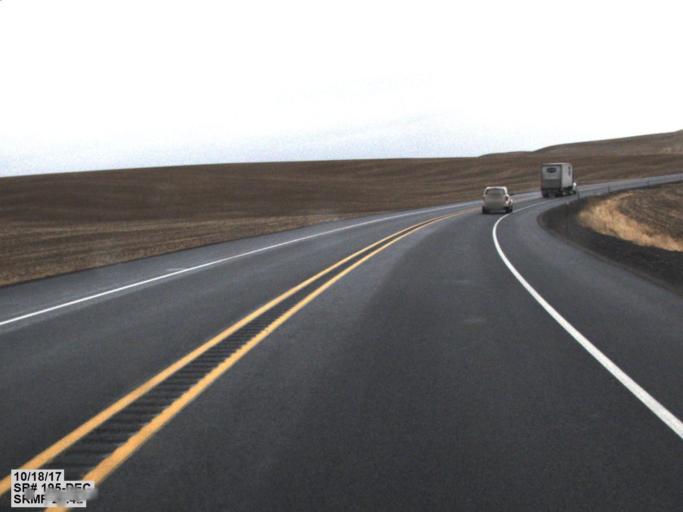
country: US
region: Washington
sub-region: Whitman County
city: Pullman
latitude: 46.7592
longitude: -117.2434
